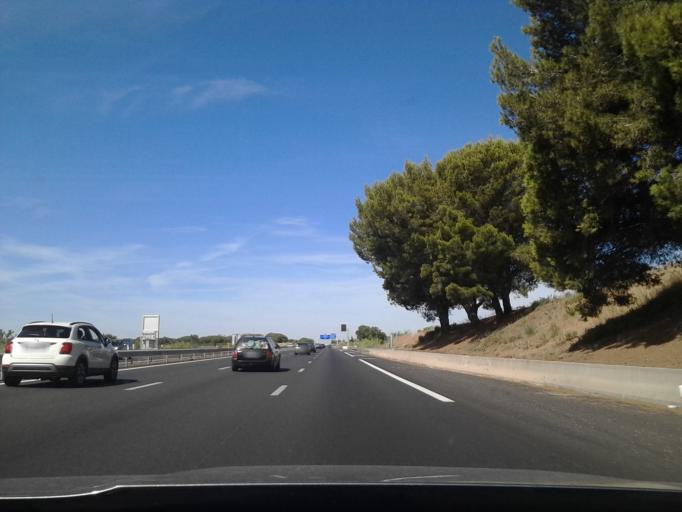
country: FR
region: Languedoc-Roussillon
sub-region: Departement de l'Herault
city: Cers
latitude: 43.3447
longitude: 3.3195
